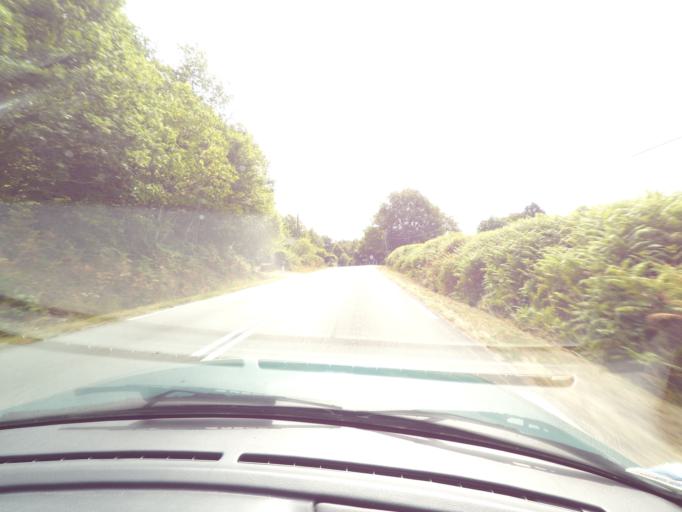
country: FR
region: Limousin
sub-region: Departement de la Haute-Vienne
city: Feytiat
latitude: 45.7983
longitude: 1.3891
